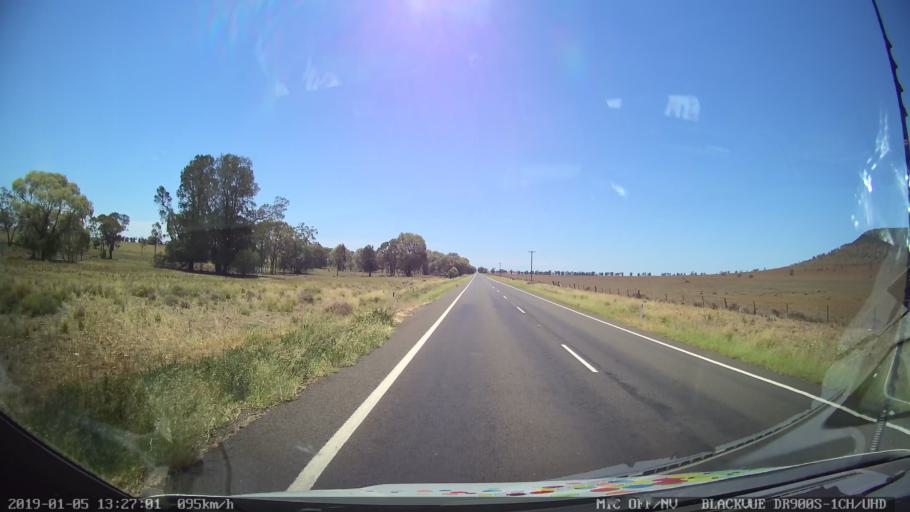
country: AU
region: New South Wales
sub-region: Gunnedah
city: Gunnedah
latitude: -31.0481
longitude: 150.0235
